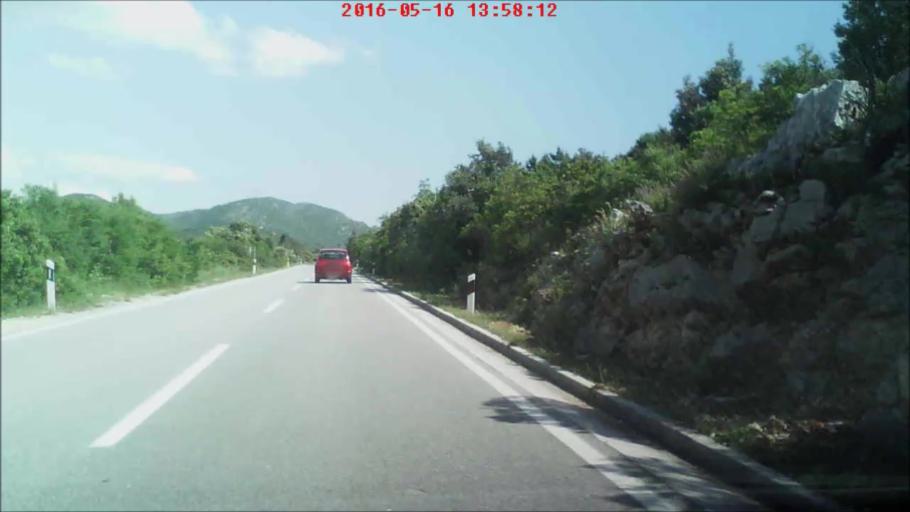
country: HR
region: Dubrovacko-Neretvanska
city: Ston
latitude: 42.8411
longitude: 17.7141
